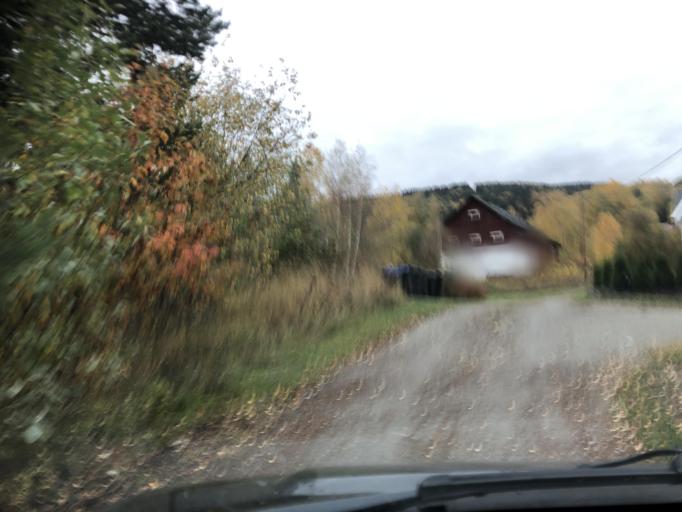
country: NO
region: Oppland
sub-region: Sor-Fron
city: Hundorp
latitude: 61.5745
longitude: 9.9138
